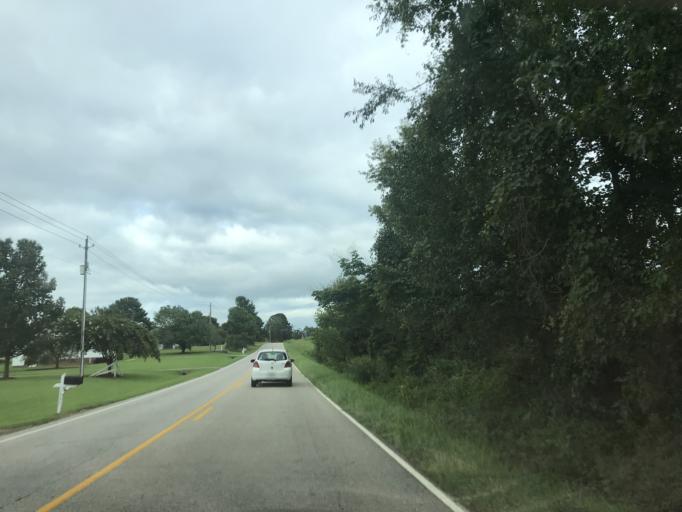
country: US
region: North Carolina
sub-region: Johnston County
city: Clayton
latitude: 35.5729
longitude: -78.5630
